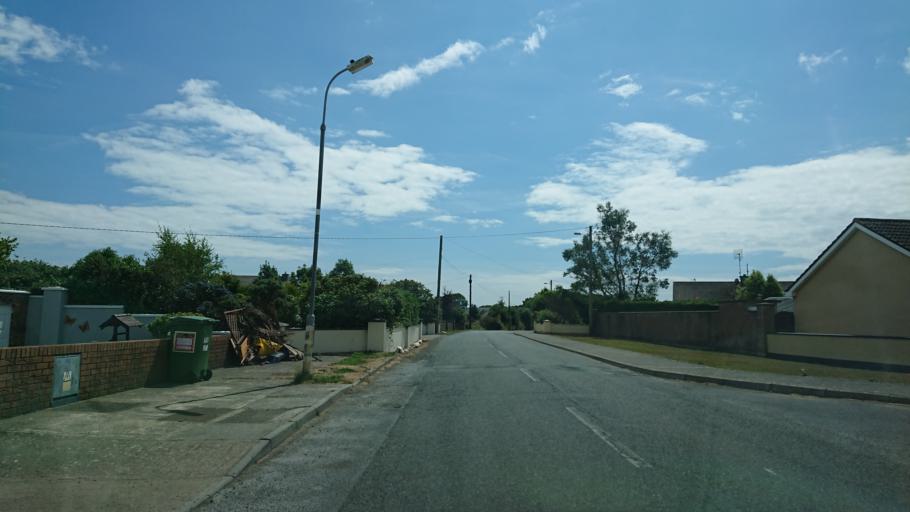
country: IE
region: Munster
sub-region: Waterford
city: Portlaw
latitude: 52.1798
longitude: -7.3343
